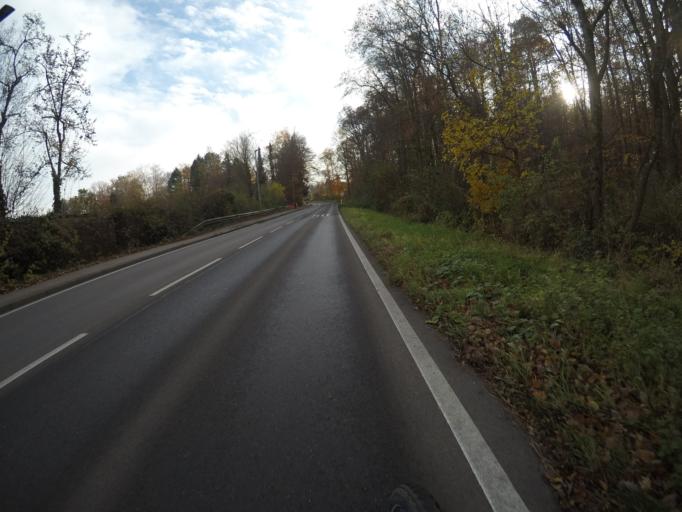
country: DE
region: Baden-Wuerttemberg
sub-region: Regierungsbezirk Stuttgart
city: Steinenbronn
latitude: 48.7080
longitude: 9.1097
